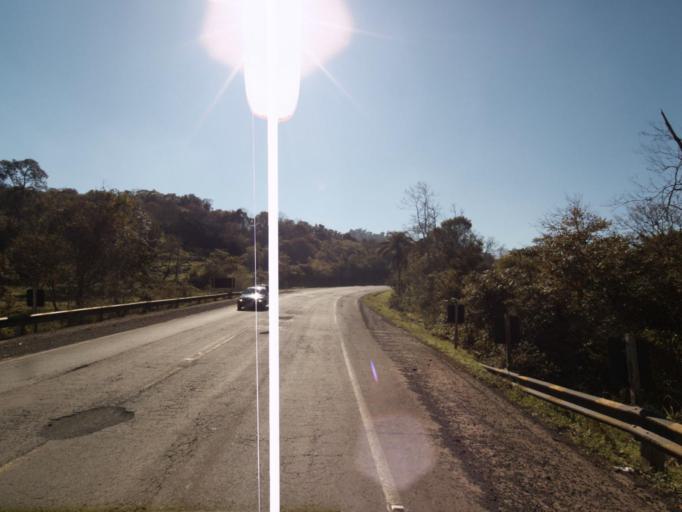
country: BR
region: Rio Grande do Sul
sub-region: Frederico Westphalen
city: Frederico Westphalen
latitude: -27.0681
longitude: -53.2283
